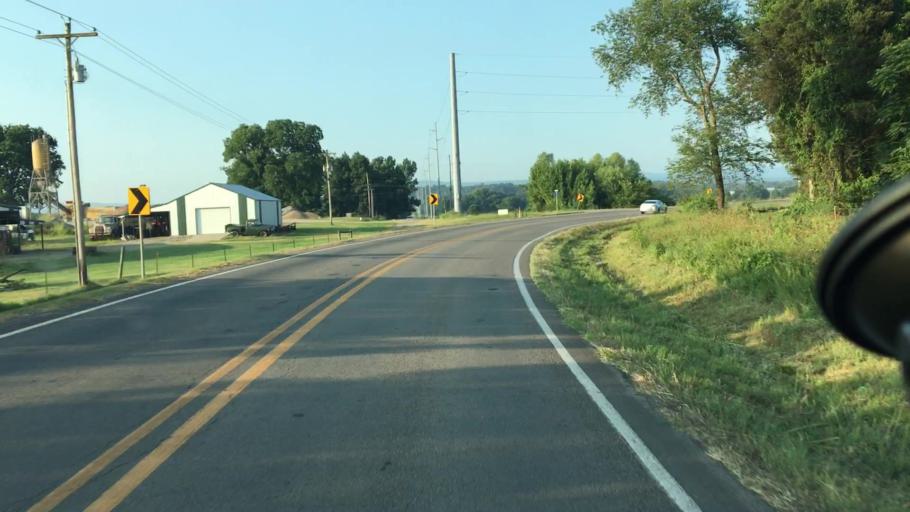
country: US
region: Arkansas
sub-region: Johnson County
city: Coal Hill
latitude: 35.3760
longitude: -93.5614
